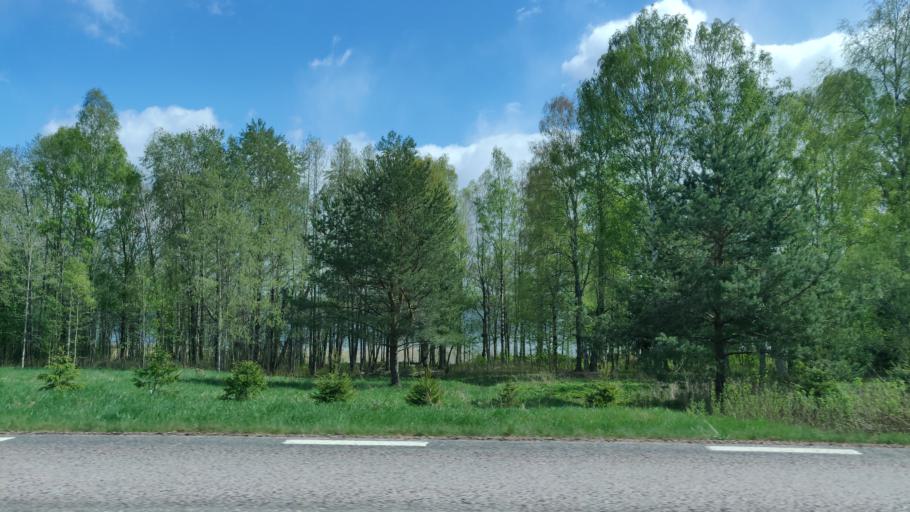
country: SE
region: Vaermland
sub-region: Karlstads Kommun
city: Skattkarr
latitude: 59.5083
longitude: 13.6154
